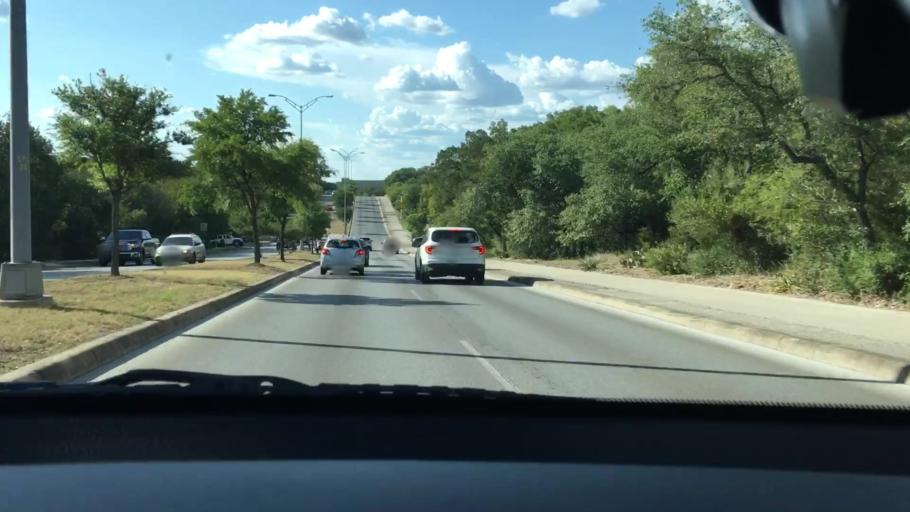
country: US
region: Texas
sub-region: Bexar County
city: Selma
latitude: 29.5858
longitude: -98.2872
